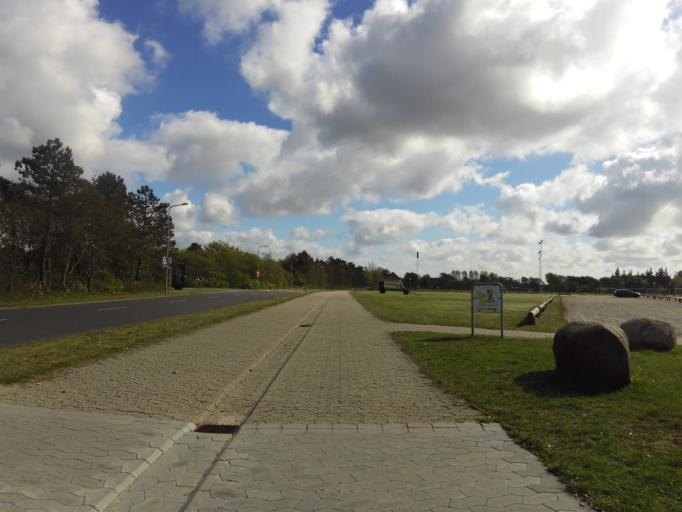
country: DK
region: South Denmark
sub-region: Esbjerg Kommune
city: Ribe
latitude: 55.2801
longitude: 8.7253
